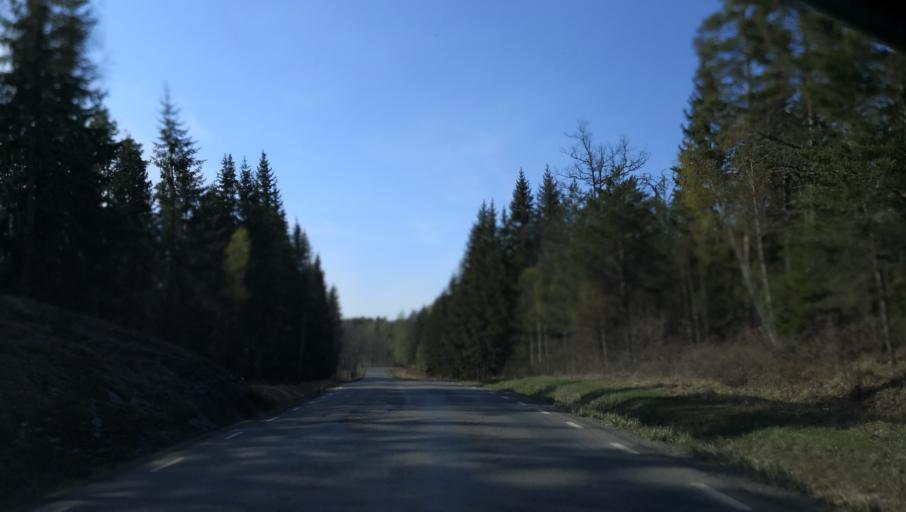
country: SE
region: Stockholm
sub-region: Varmdo Kommun
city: Holo
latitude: 59.3047
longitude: 18.5926
